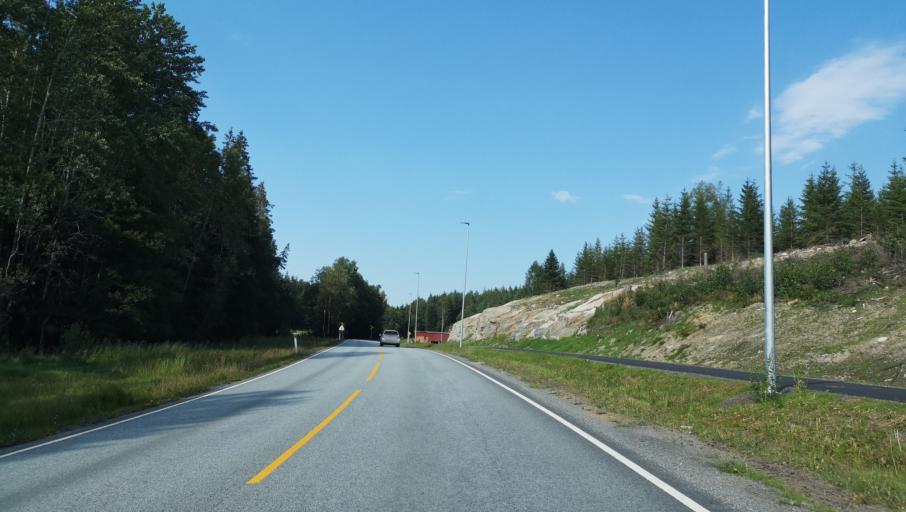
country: NO
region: Ostfold
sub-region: Valer
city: Kirkebygda
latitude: 59.4872
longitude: 10.8055
